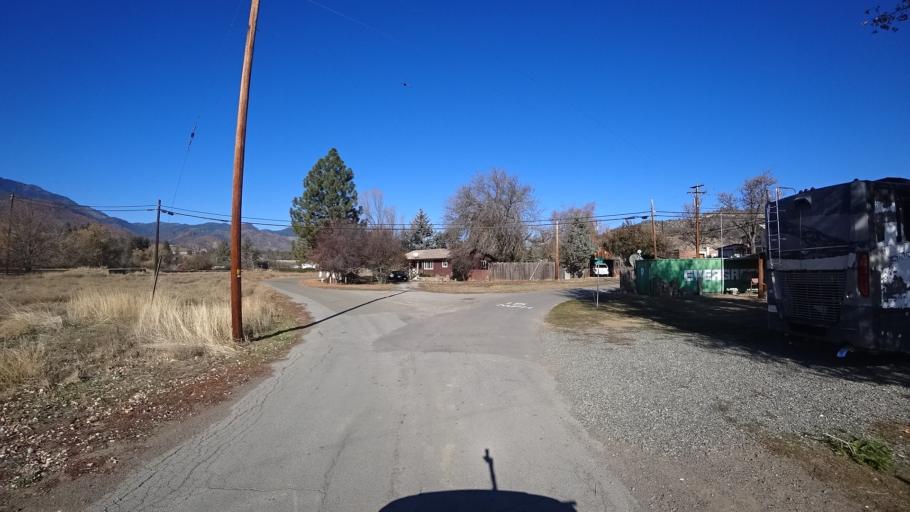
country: US
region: California
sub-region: Siskiyou County
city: Montague
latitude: 41.9110
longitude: -122.5551
